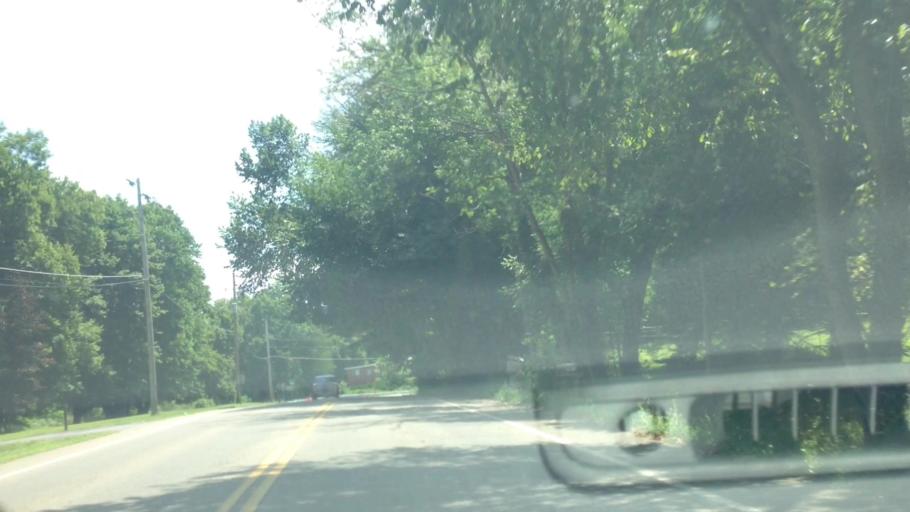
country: US
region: Ohio
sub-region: Summit County
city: Clinton
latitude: 40.9490
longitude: -81.6311
